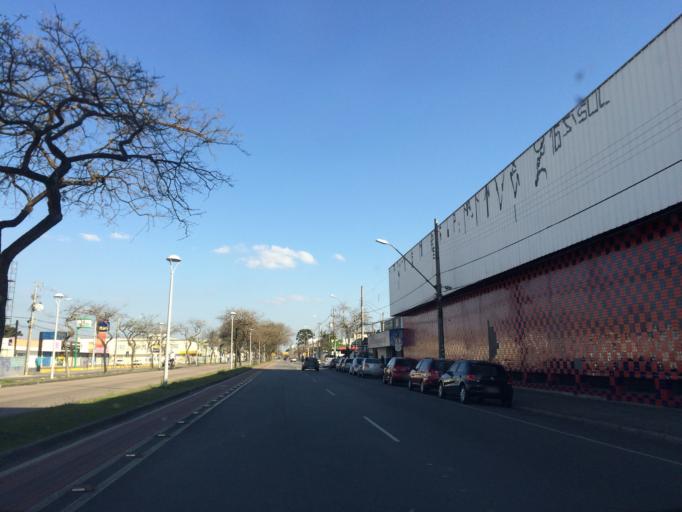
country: BR
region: Parana
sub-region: Sao Jose Dos Pinhais
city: Sao Jose dos Pinhais
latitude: -25.4924
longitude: -49.2421
